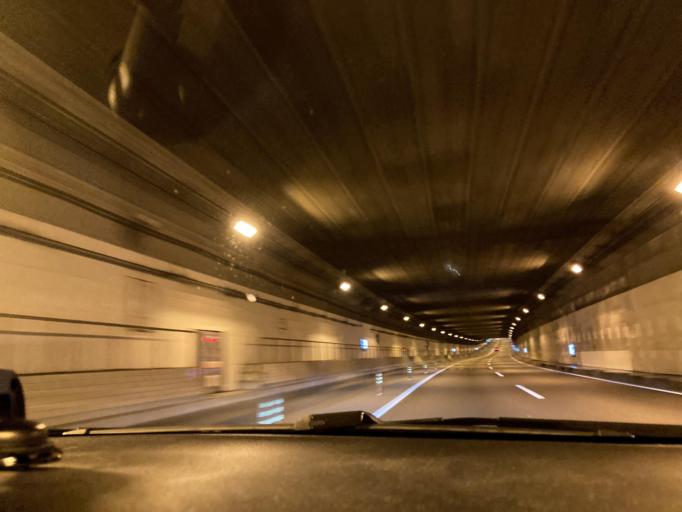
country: JP
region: Okinawa
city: Naha-shi
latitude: 26.2153
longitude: 127.6602
